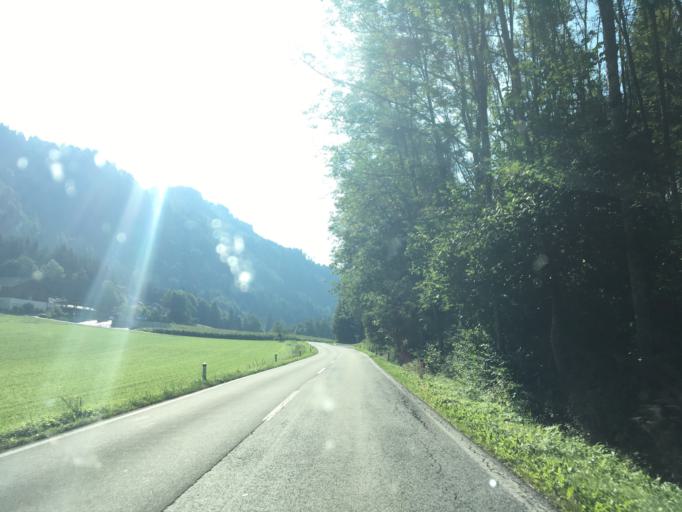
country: AT
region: Carinthia
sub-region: Politischer Bezirk Sankt Veit an der Glan
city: Bruckl
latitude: 46.7225
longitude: 14.5514
